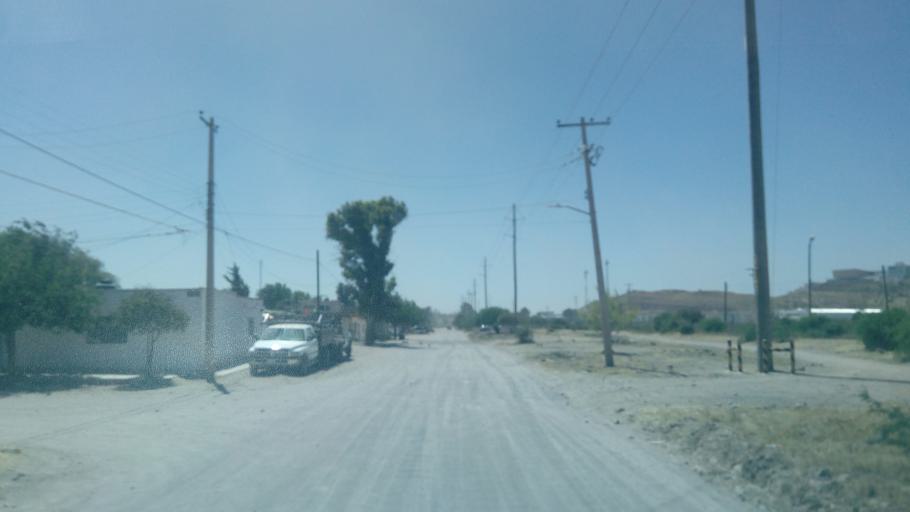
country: MX
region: Durango
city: Victoria de Durango
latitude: 24.0762
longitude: -104.6584
